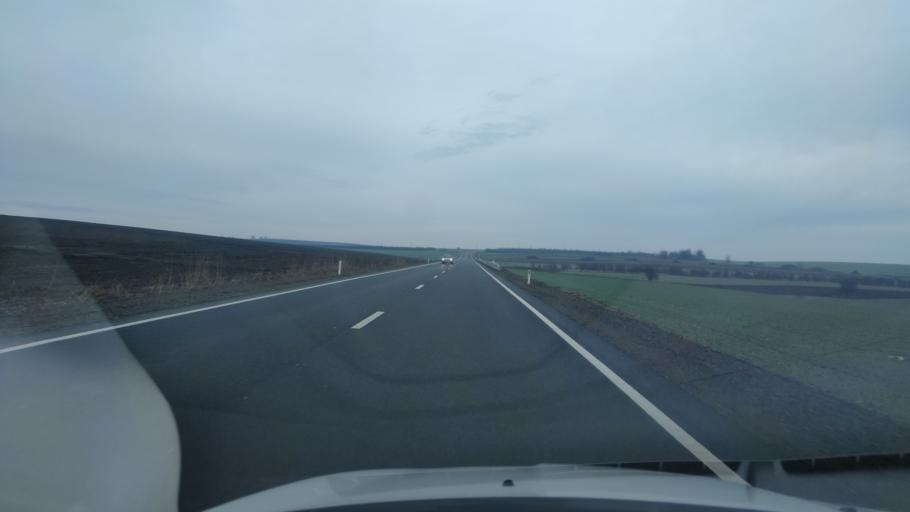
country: RO
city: Szekelyhid
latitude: 47.3306
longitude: 22.0914
